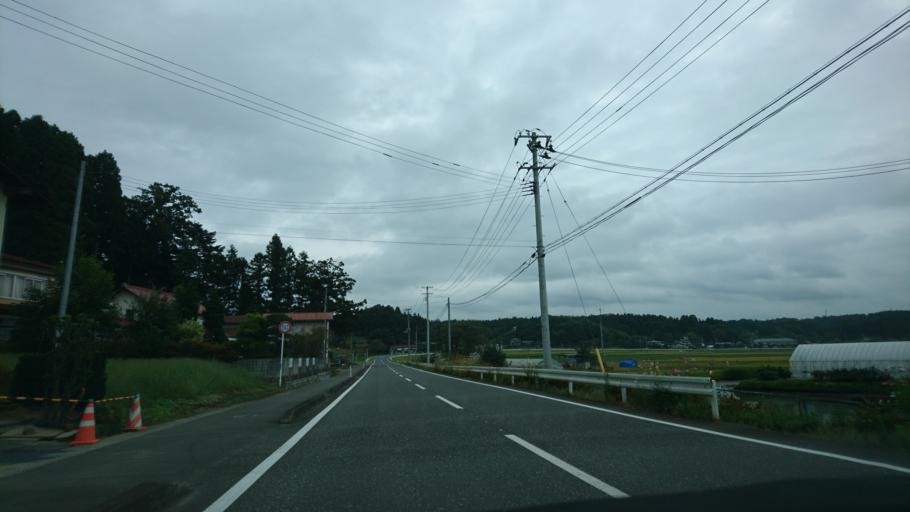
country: JP
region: Iwate
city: Ichinoseki
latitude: 38.8034
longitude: 141.1056
